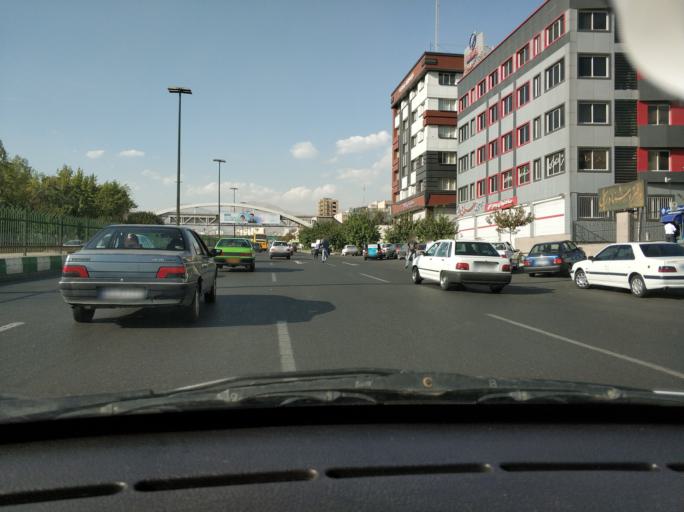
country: IR
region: Tehran
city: Tehran
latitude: 35.7046
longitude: 51.3375
